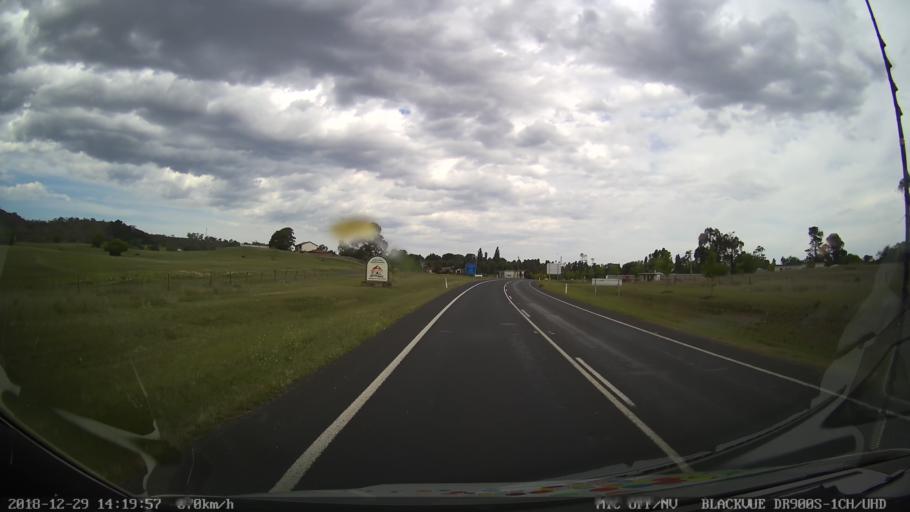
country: AU
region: New South Wales
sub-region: Cooma-Monaro
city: Cooma
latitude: -36.5040
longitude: 149.2846
